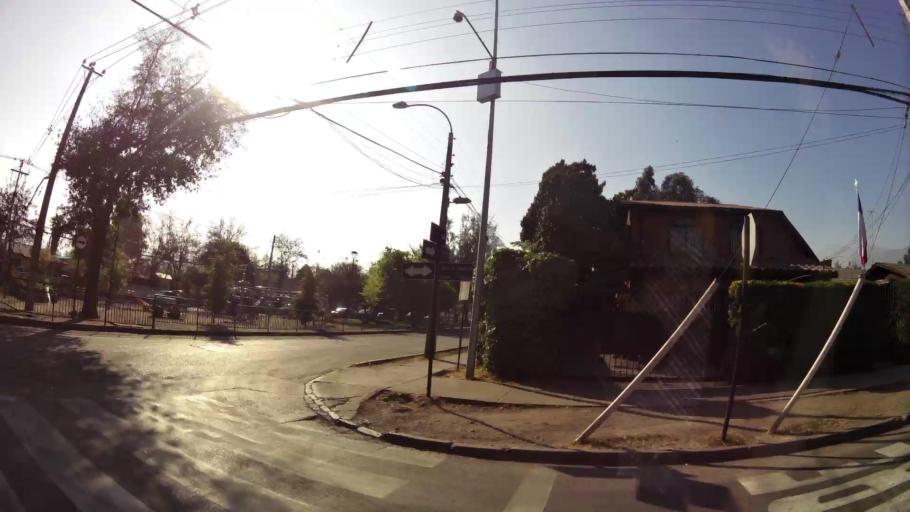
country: CL
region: Santiago Metropolitan
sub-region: Provincia de Santiago
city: Villa Presidente Frei, Nunoa, Santiago, Chile
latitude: -33.3544
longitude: -70.5076
